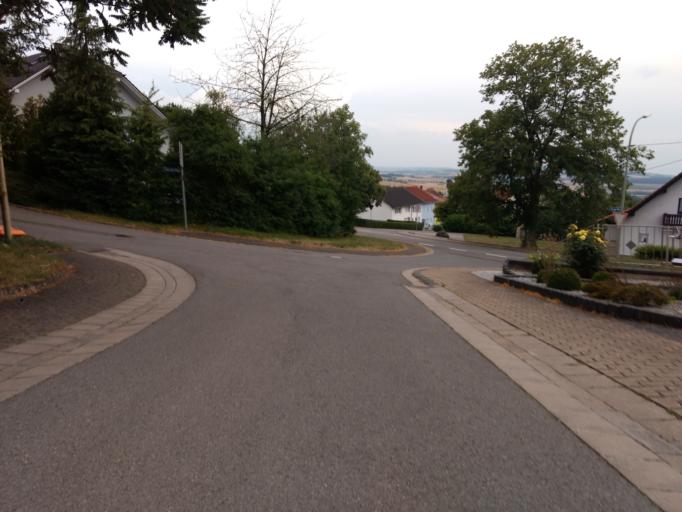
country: DE
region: Saarland
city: Rehlingen-Siersburg
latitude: 49.3205
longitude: 6.6535
